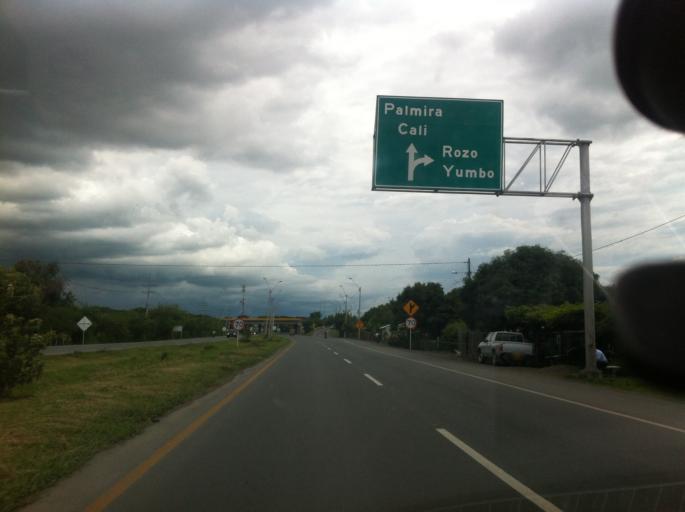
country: CO
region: Valle del Cauca
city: El Cerrito
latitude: 3.7043
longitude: -76.3196
